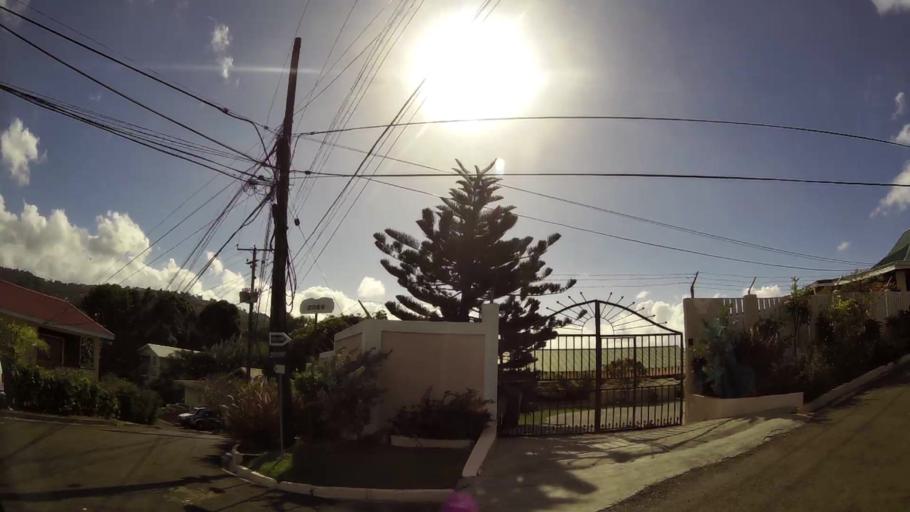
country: LC
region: Castries Quarter
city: Bisee
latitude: 14.0173
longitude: -60.9935
